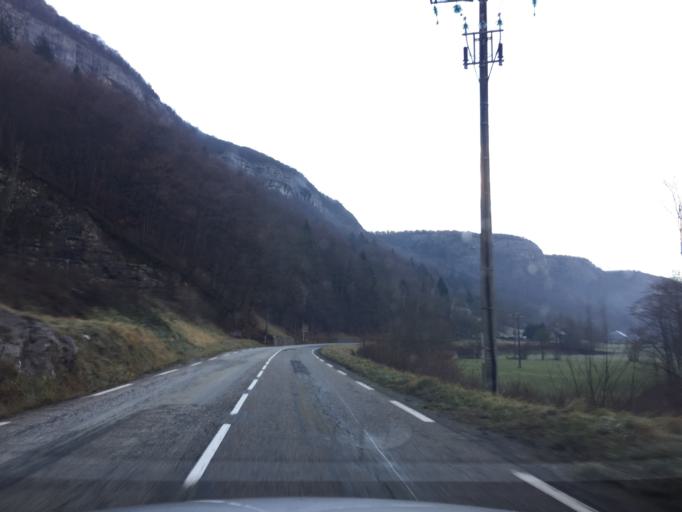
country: FR
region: Rhone-Alpes
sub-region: Departement de la Haute-Savoie
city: Gruffy
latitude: 45.7434
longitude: 6.0969
